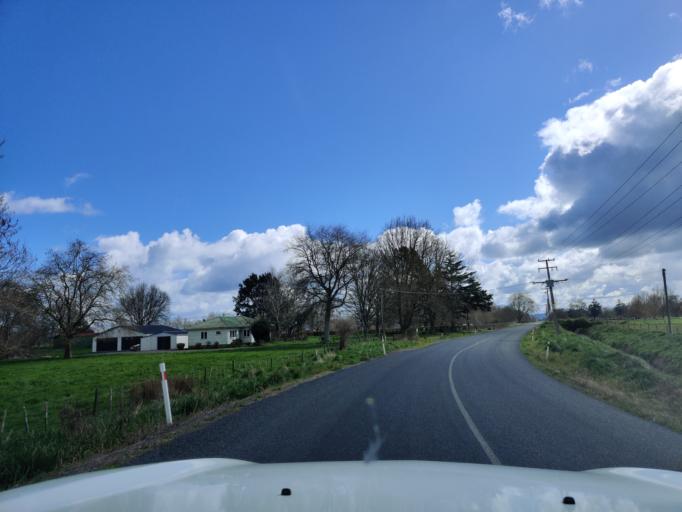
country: NZ
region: Waikato
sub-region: Waikato District
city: Ngaruawahia
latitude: -37.6163
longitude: 175.3152
